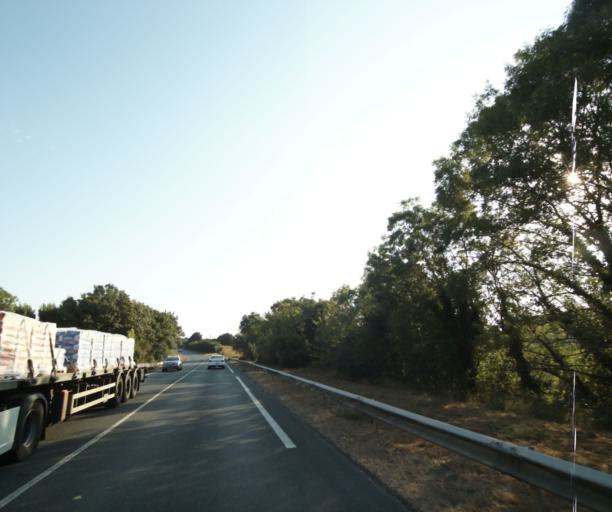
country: FR
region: Poitou-Charentes
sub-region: Departement de la Charente-Maritime
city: Cabariot
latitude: 45.9315
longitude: -0.8701
